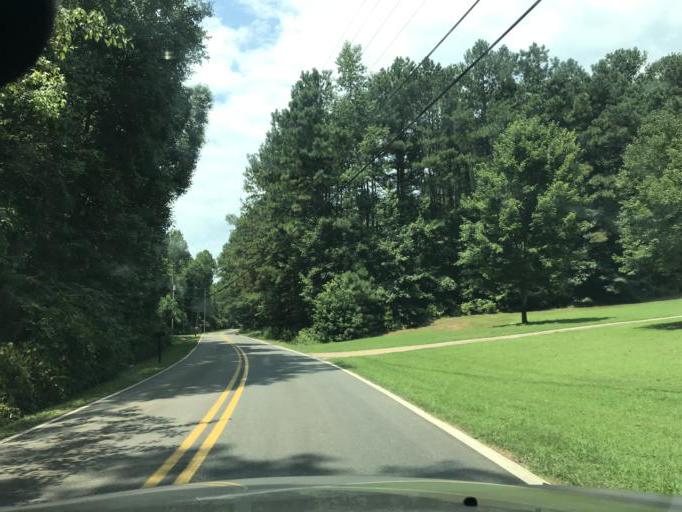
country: US
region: Georgia
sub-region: Dawson County
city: Dawsonville
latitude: 34.3328
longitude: -84.1801
